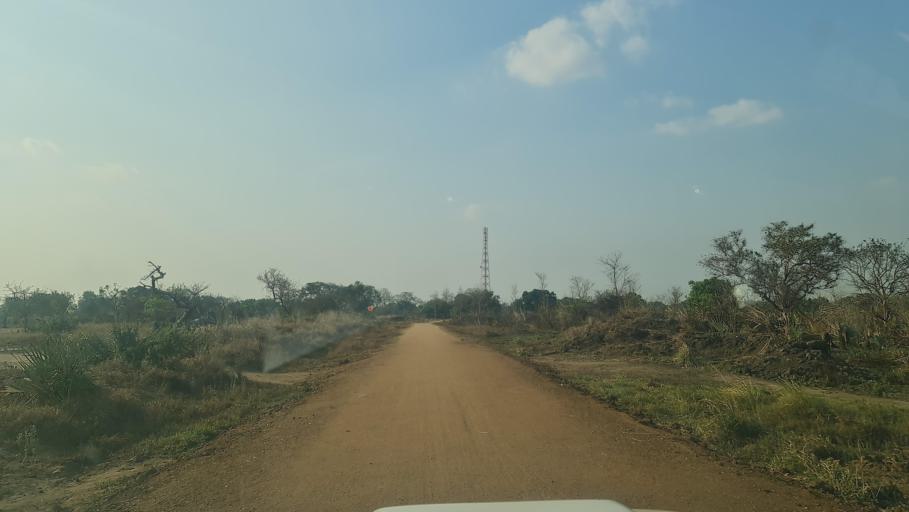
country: MZ
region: Zambezia
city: Quelimane
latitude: -18.1473
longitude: 35.9874
